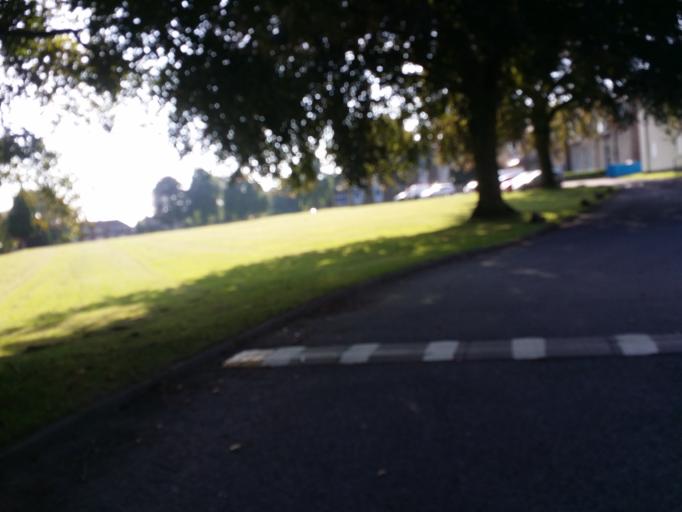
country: GB
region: England
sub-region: City of York
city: Heslington
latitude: 53.9518
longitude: -1.0623
